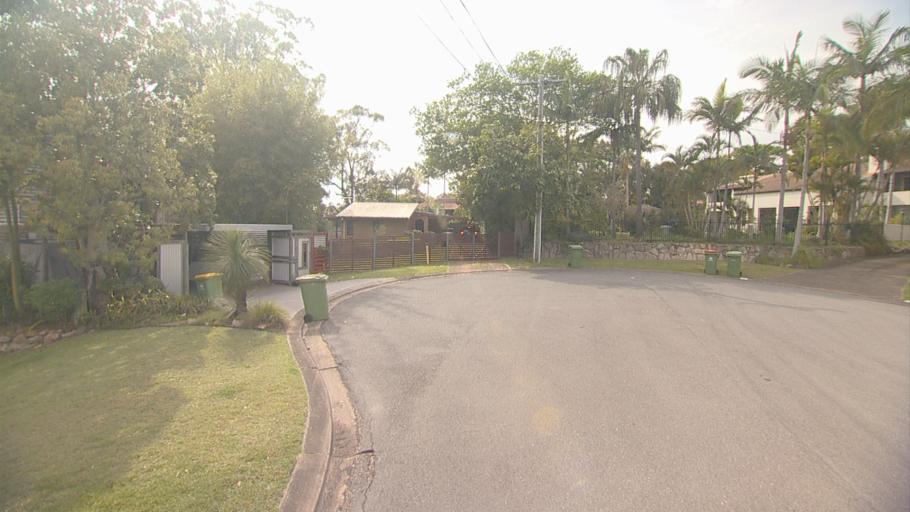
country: AU
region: Queensland
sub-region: Logan
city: Springwood
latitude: -27.6193
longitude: 153.1431
